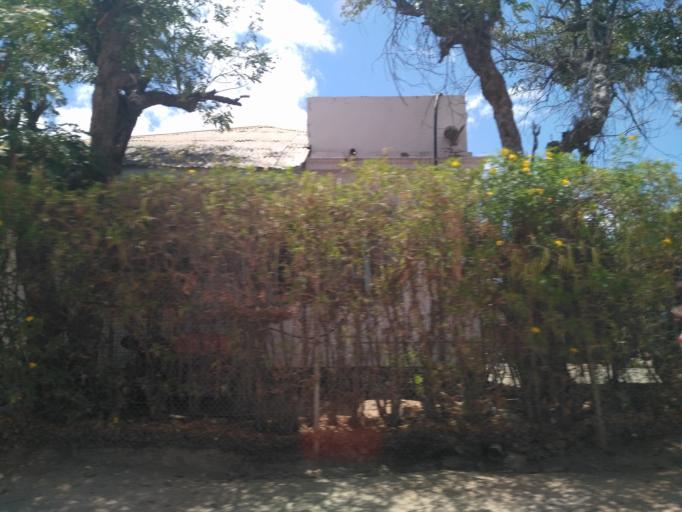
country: TZ
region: Dodoma
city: Dodoma
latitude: -6.1850
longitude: 35.7478
